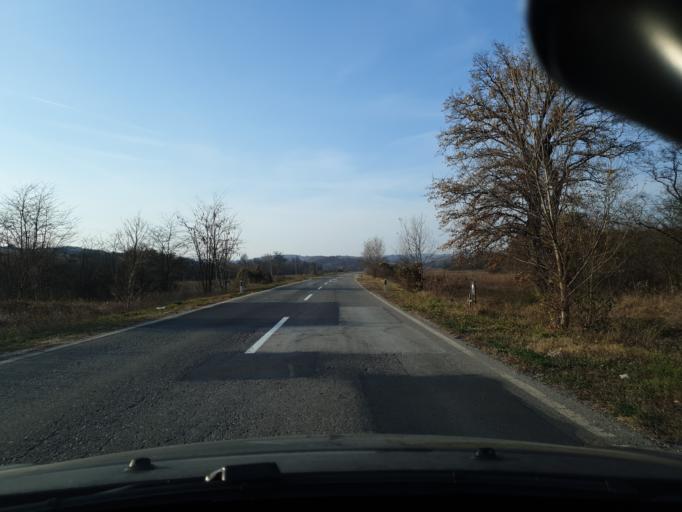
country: RS
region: Central Serbia
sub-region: Zajecarski Okrug
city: Zajecar
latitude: 43.9508
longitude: 22.2858
